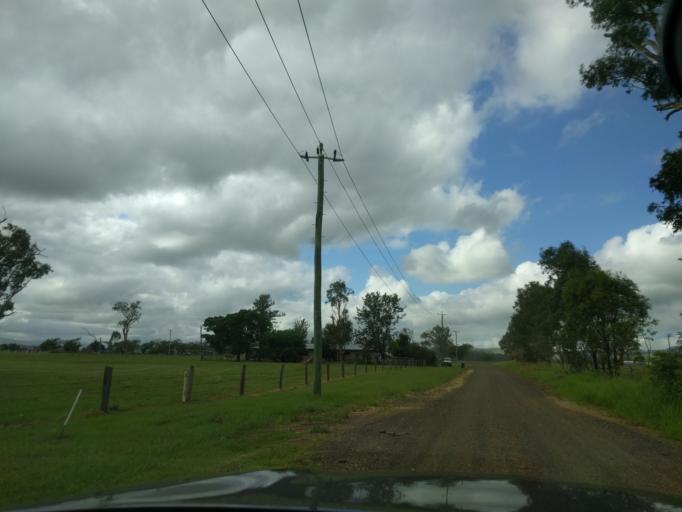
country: AU
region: Queensland
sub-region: Logan
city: Cedar Vale
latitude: -28.0067
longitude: 152.9959
